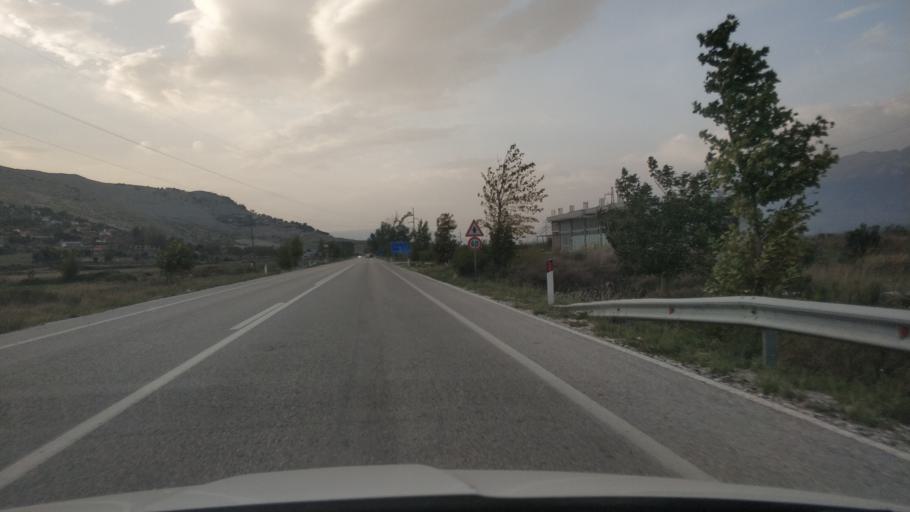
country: AL
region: Gjirokaster
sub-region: Rrethi i Gjirokastres
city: Libohove
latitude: 39.9620
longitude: 20.2441
